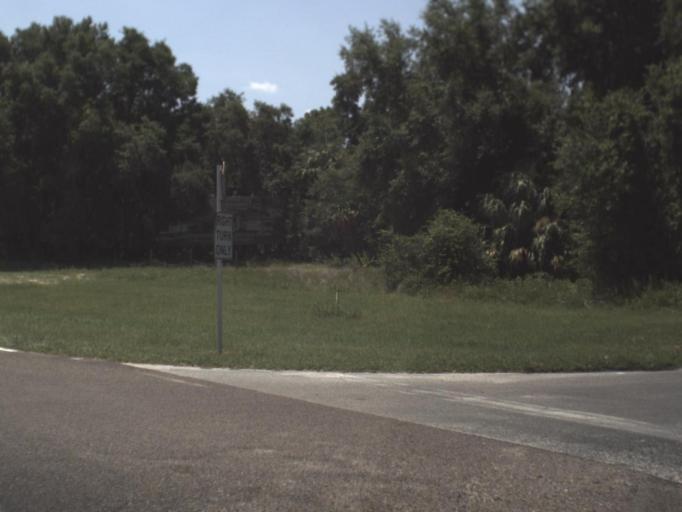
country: US
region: Florida
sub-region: Citrus County
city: Homosassa Springs
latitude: 28.7944
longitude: -82.5728
